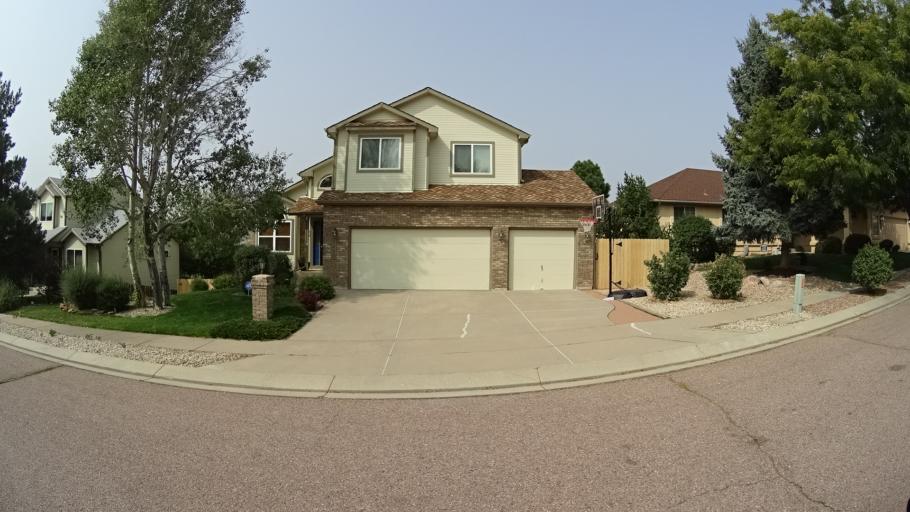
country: US
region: Colorado
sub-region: El Paso County
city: Cimarron Hills
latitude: 38.9157
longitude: -104.7399
